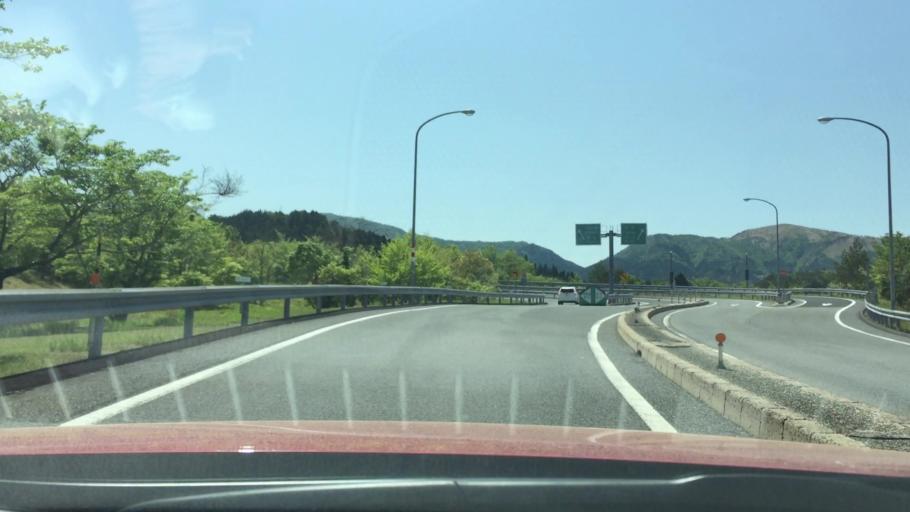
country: JP
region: Tottori
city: Kurayoshi
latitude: 35.2728
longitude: 133.6189
